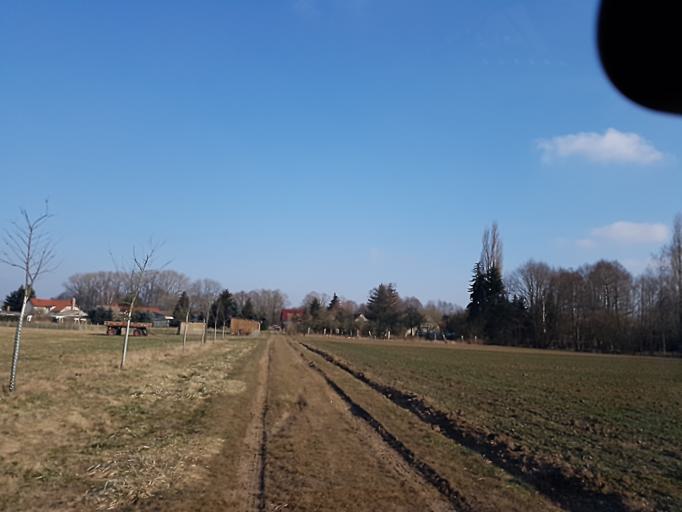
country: DE
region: Brandenburg
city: Ruckersdorf
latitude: 51.5969
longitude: 13.5444
